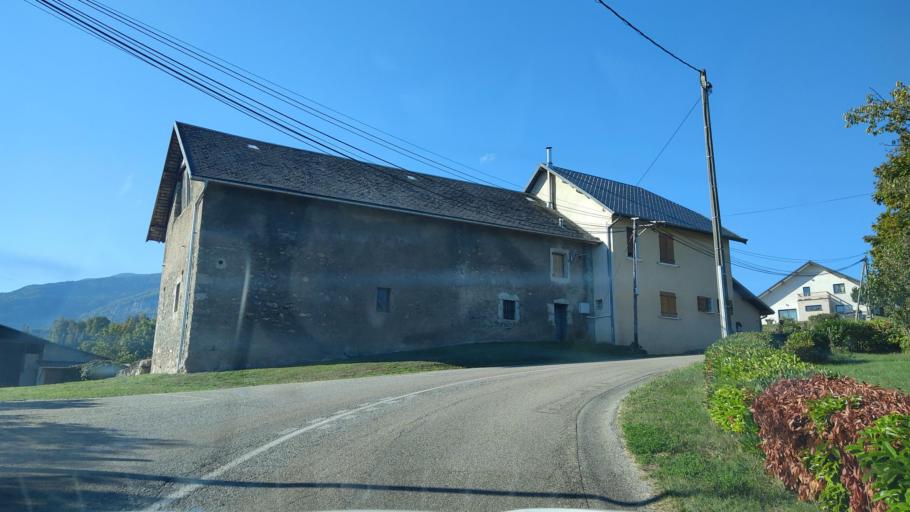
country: FR
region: Rhone-Alpes
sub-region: Departement de la Savoie
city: Jacob-Bellecombette
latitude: 45.5404
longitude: 5.9131
